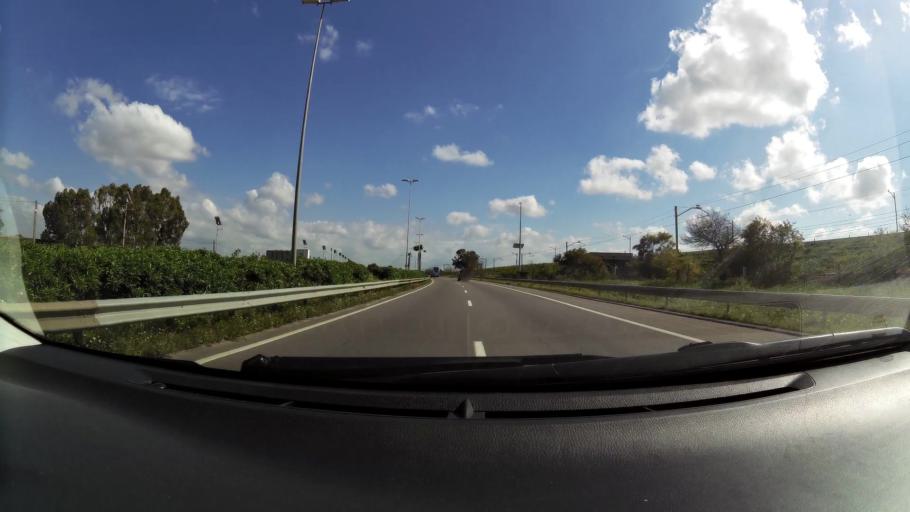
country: MA
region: Chaouia-Ouardigha
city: Nouaseur
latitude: 33.4106
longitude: -7.6262
